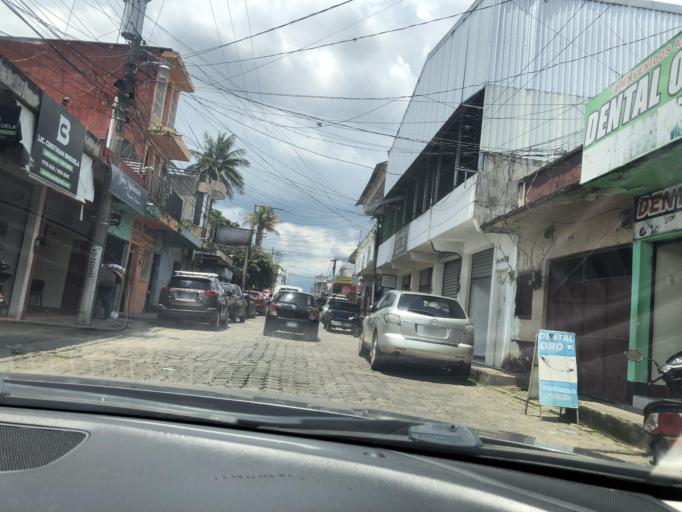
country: GT
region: Quetzaltenango
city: Coatepeque
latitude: 14.7029
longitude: -91.8658
